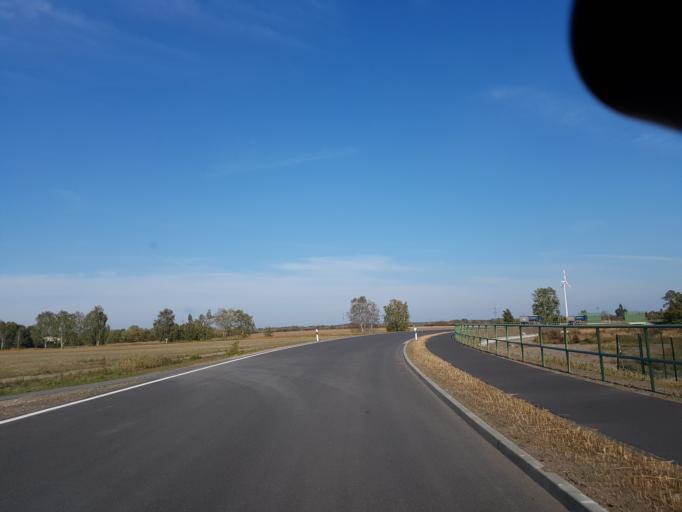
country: DE
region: Brandenburg
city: Finsterwalde
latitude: 51.6428
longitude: 13.7143
